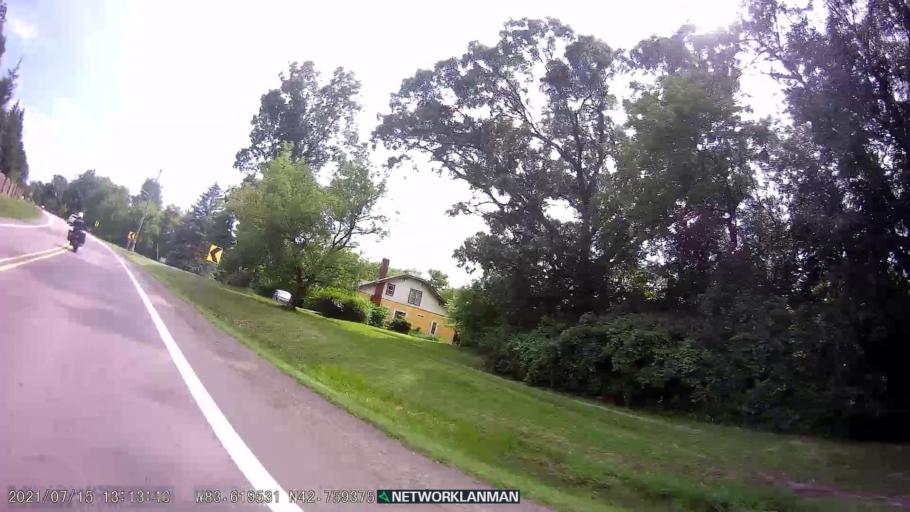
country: US
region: Michigan
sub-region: Oakland County
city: Holly
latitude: 42.7591
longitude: -83.6194
